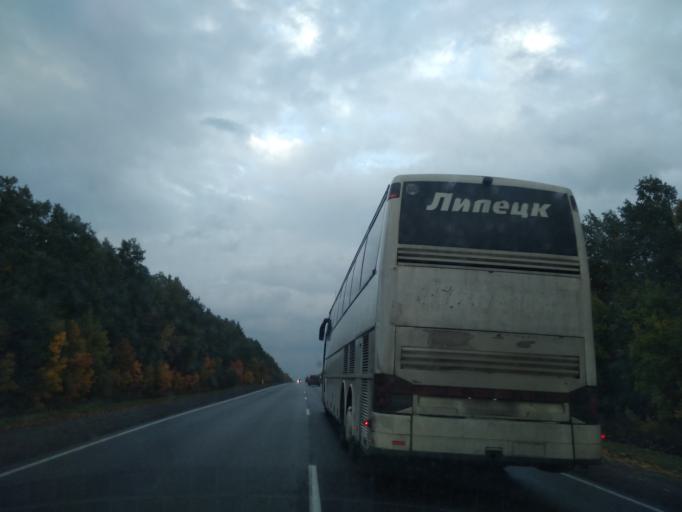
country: RU
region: Lipetsk
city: Borinskoye
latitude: 52.5975
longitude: 39.3010
